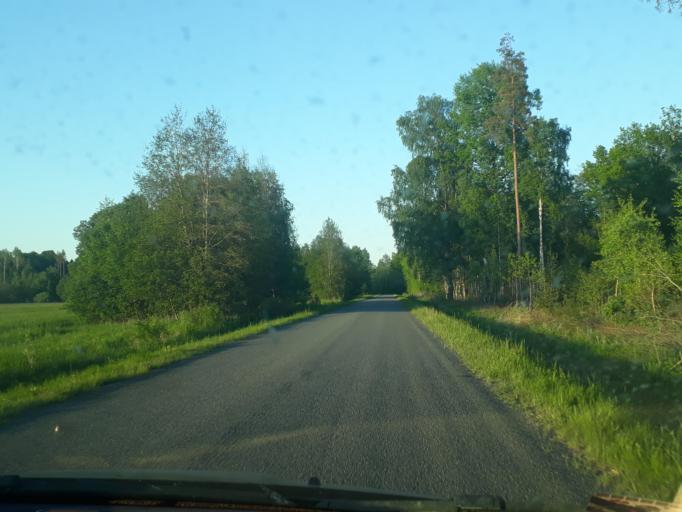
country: EE
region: Paernumaa
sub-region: Vaendra vald (alev)
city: Vandra
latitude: 58.5641
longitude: 24.9711
